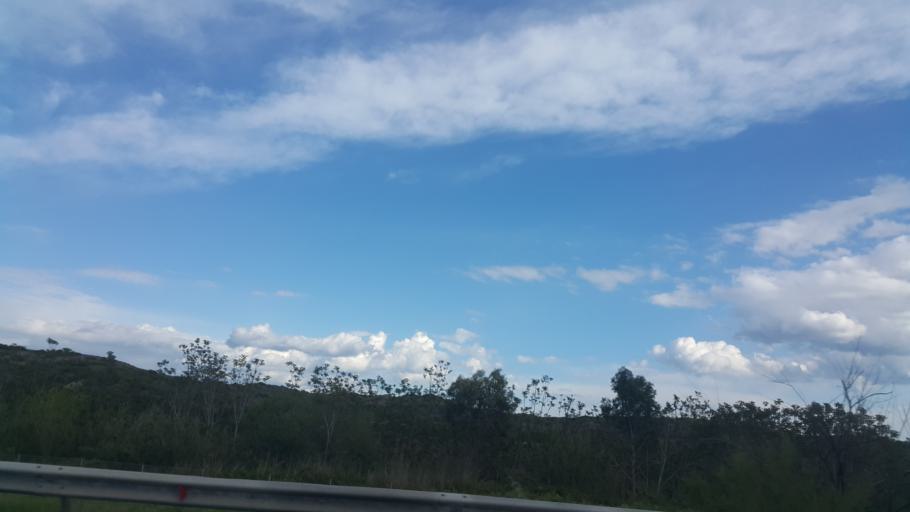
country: TR
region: Adana
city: Ceyhan
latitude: 36.9954
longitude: 35.9149
